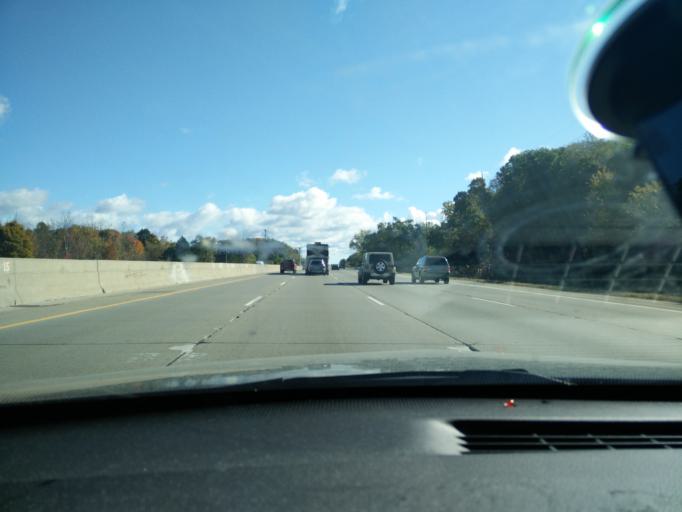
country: US
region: Michigan
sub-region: Oakland County
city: Farmington Hills
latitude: 42.4934
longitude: -83.4064
